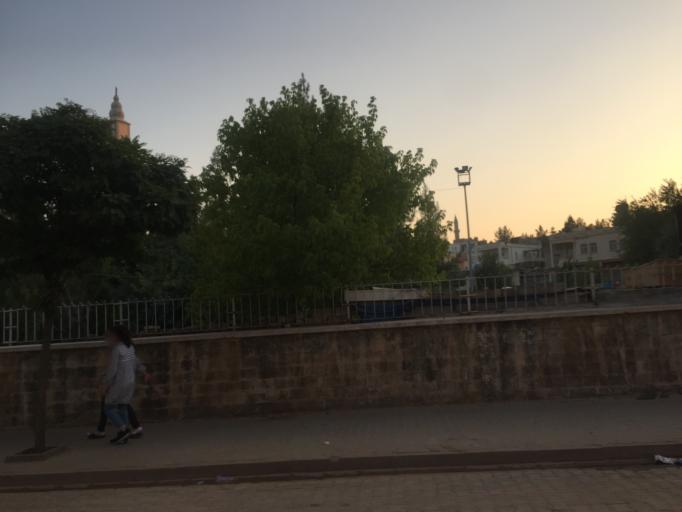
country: TR
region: Mardin
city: Midyat
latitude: 37.4284
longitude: 41.3389
